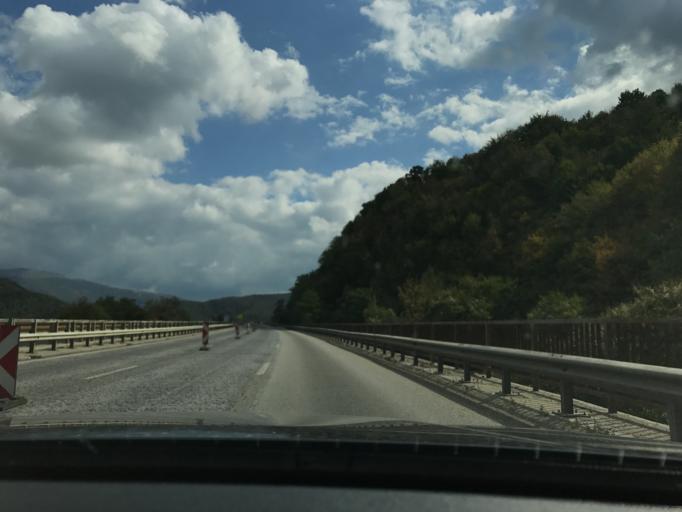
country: BG
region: Sofiya
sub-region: Obshtina Botevgrad
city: Botevgrad
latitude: 42.8108
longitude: 23.8007
